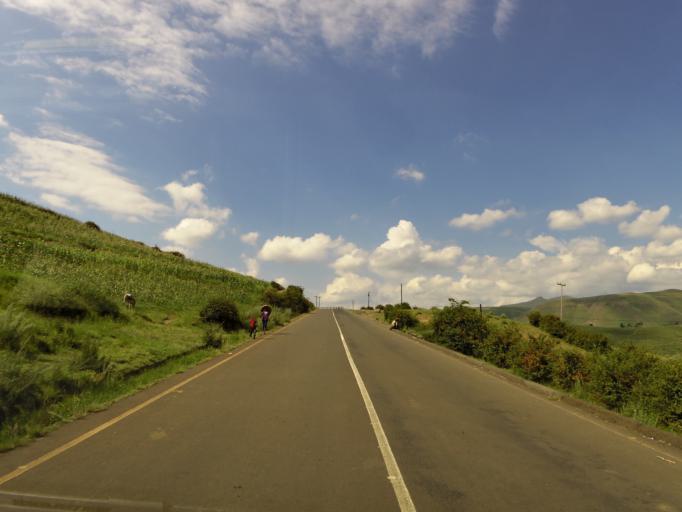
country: LS
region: Thaba-Tseka
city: Thaba-Tseka
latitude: -29.1221
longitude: 28.4920
